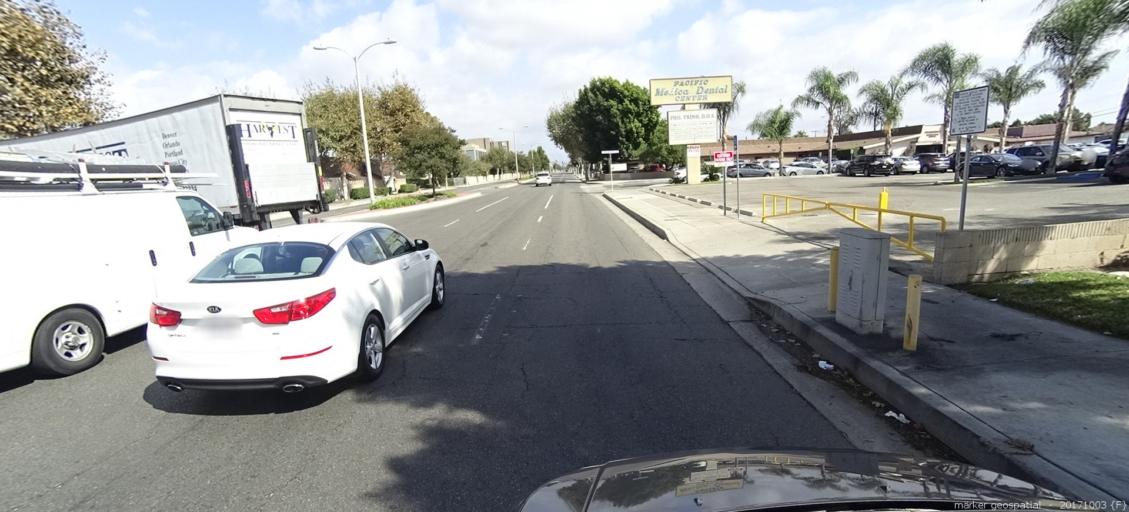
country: US
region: California
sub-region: Orange County
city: Garden Grove
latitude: 33.7743
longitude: -117.9184
